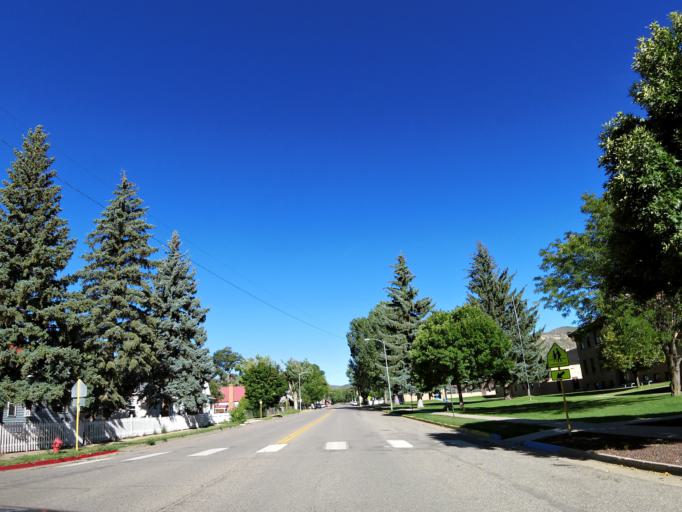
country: US
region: Colorado
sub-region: Montezuma County
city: Mancos
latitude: 37.3451
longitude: -108.2932
